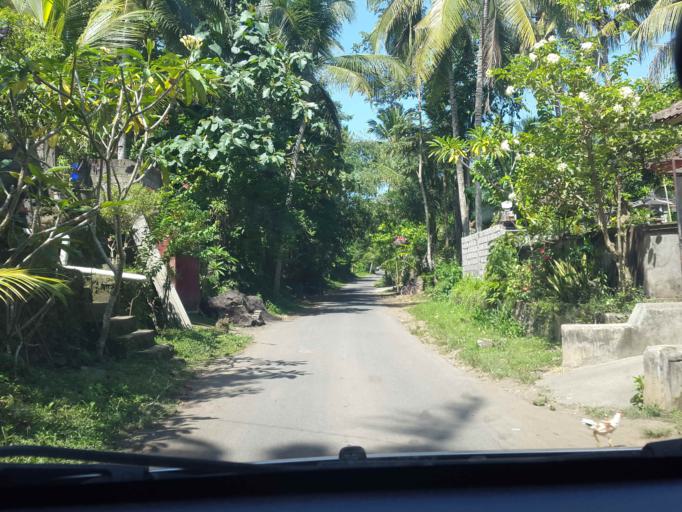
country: ID
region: Bali
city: Dawan
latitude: -8.5334
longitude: 115.4475
